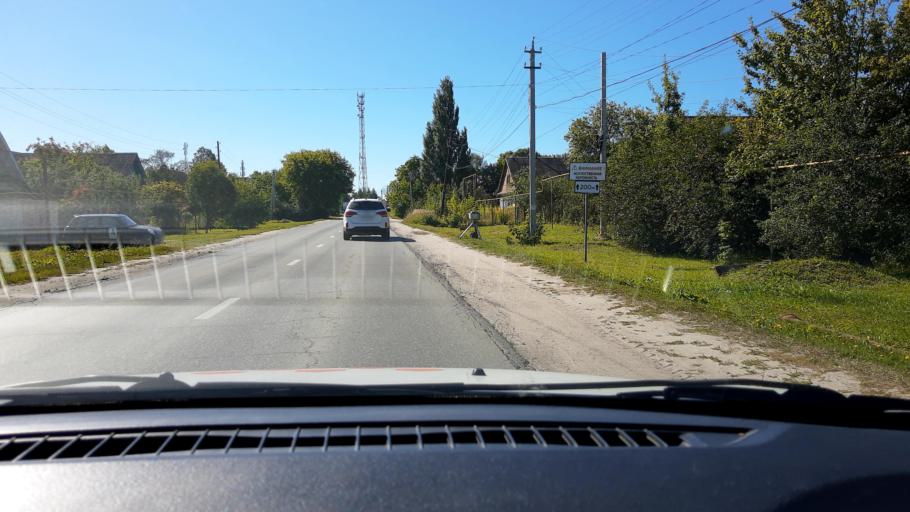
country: RU
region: Nizjnij Novgorod
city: Zavolzh'ye
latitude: 56.7188
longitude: 43.4141
